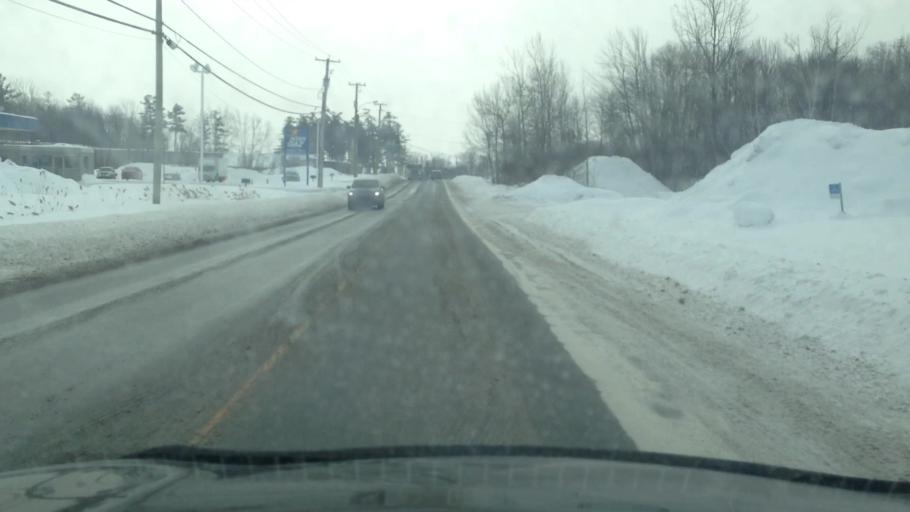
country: CA
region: Quebec
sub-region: Laurentides
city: Saint-Jerome
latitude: 45.7826
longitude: -74.0294
